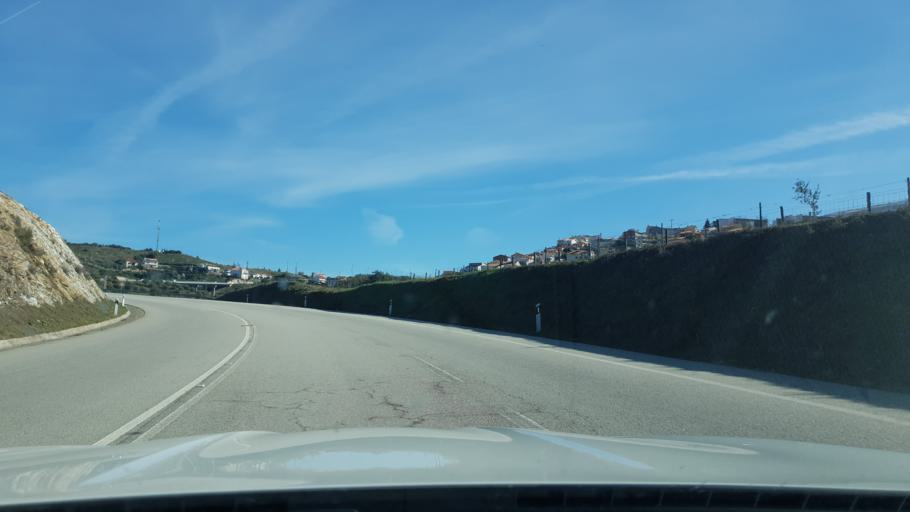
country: PT
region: Braganca
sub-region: Torre de Moncorvo
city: Torre de Moncorvo
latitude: 41.1770
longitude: -7.0642
